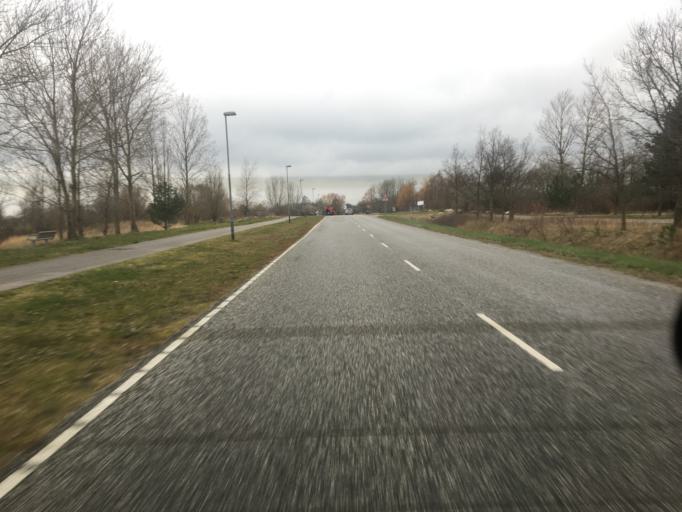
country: DK
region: Capital Region
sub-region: Vallensbaek Kommune
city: Vallensbaek
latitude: 55.6142
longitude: 12.3966
